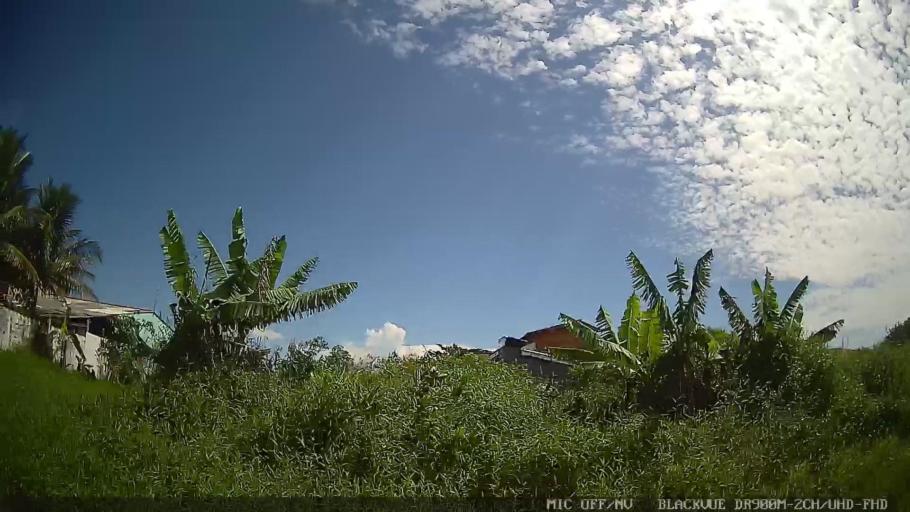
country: BR
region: Sao Paulo
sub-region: Iguape
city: Iguape
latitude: -24.7261
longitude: -47.5128
